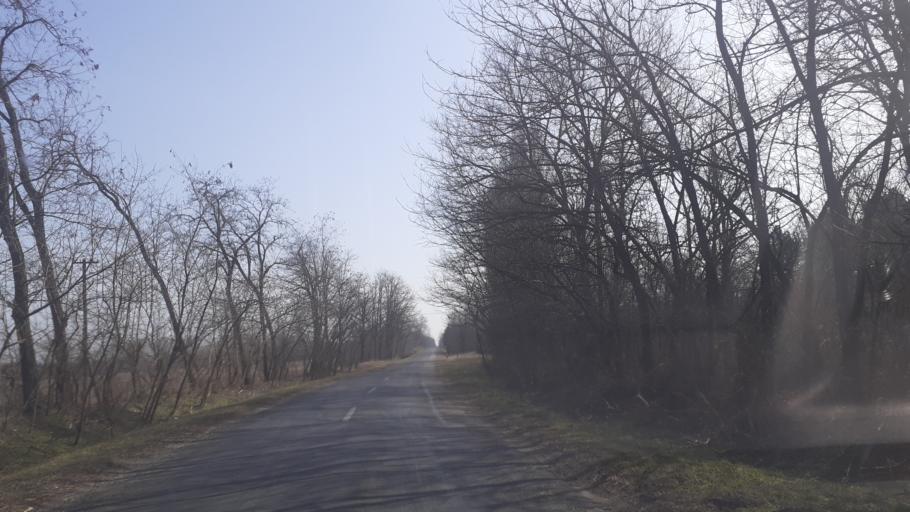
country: HU
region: Pest
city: Orkeny
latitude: 47.0728
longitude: 19.3813
